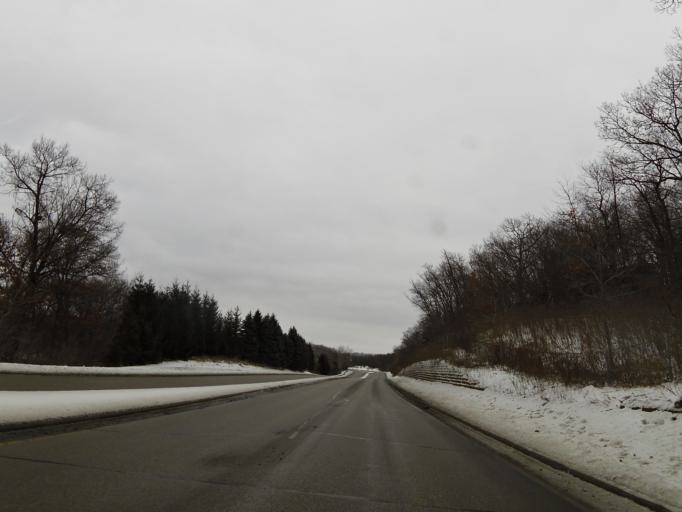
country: US
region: Minnesota
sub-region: Dakota County
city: Apple Valley
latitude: 44.7562
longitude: -93.2300
